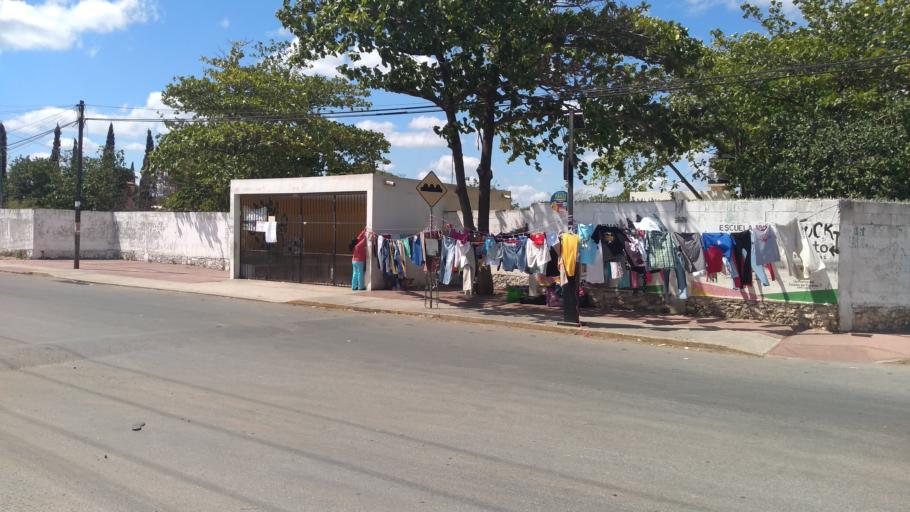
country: MX
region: Yucatan
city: Itzincab Palomeque
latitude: 20.9260
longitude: -89.6728
